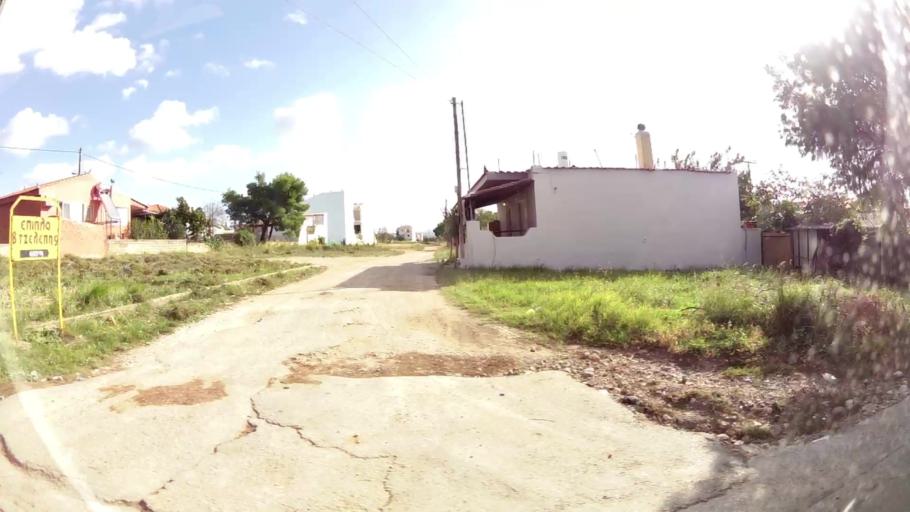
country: GR
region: Attica
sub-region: Nomarchia Anatolikis Attikis
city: Thrakomakedones
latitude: 38.1182
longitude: 23.7562
